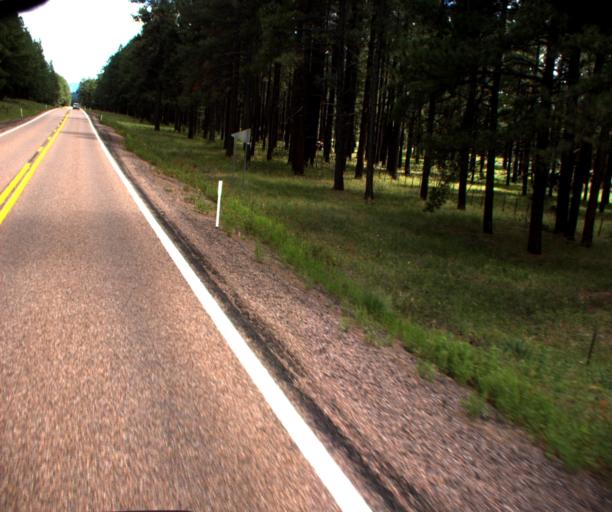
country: US
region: Arizona
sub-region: Navajo County
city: Pinetop-Lakeside
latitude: 34.0608
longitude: -109.7677
